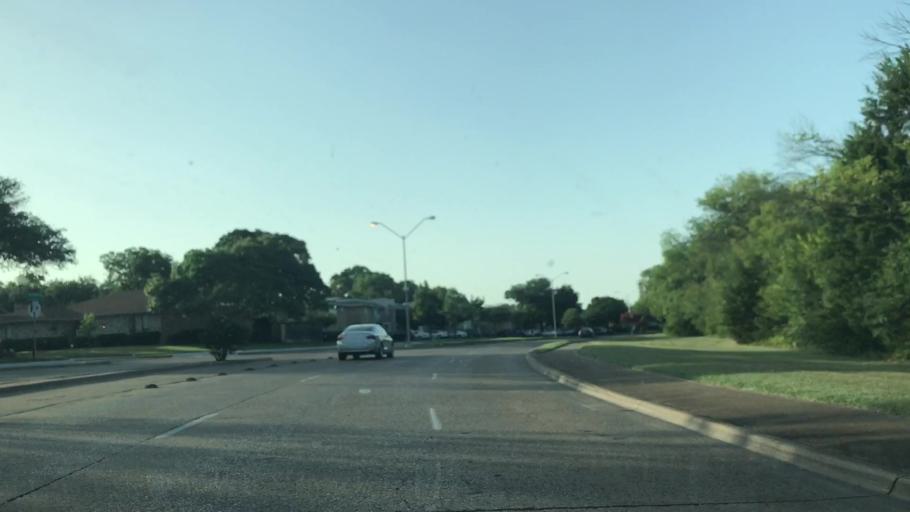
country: US
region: Texas
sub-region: Dallas County
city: Garland
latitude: 32.8601
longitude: -96.7015
